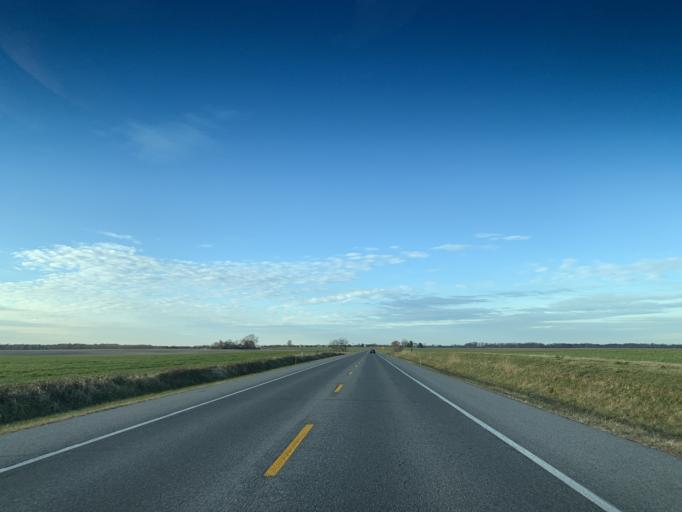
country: US
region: Maryland
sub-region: Kent County
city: Chestertown
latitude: 39.2426
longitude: -76.0691
